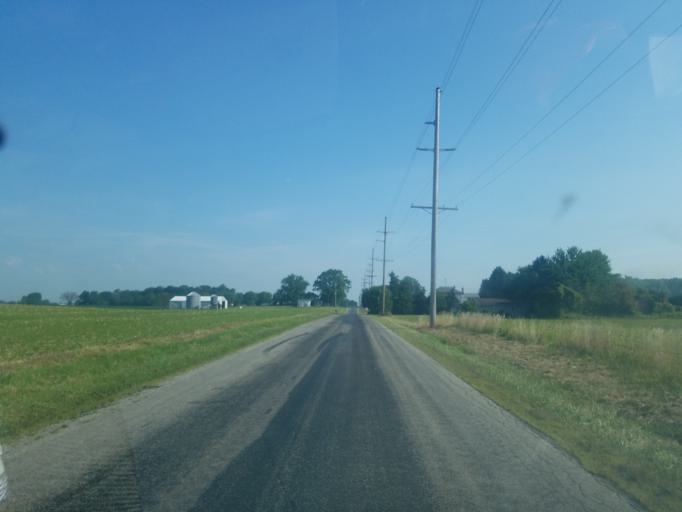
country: US
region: Ohio
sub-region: Huron County
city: Plymouth
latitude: 40.9393
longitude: -82.6859
